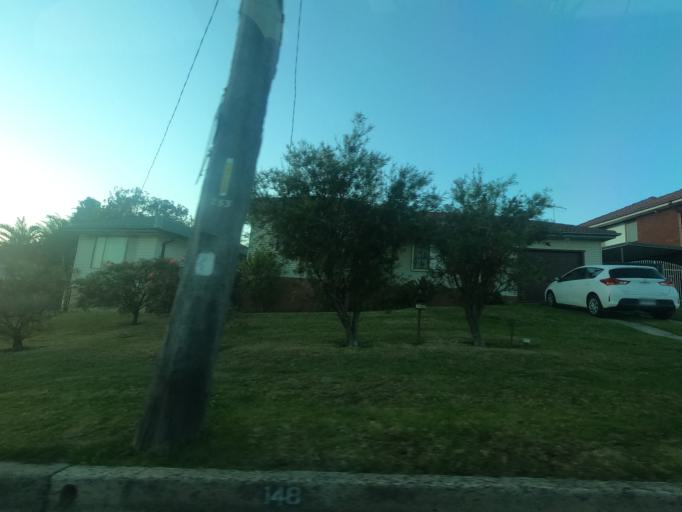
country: AU
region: New South Wales
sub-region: Wollongong
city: Koonawarra
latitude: -34.5052
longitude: 150.8004
